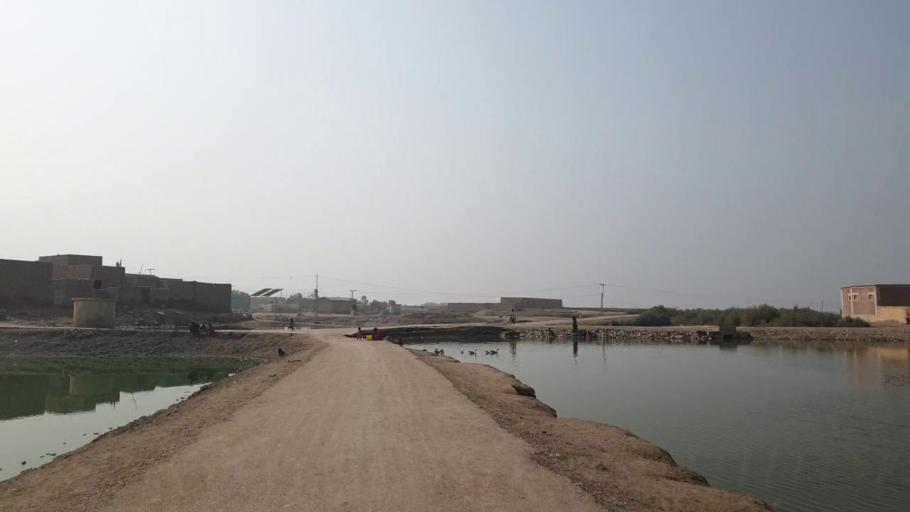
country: PK
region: Sindh
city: Bhan
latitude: 26.4465
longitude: 67.7153
